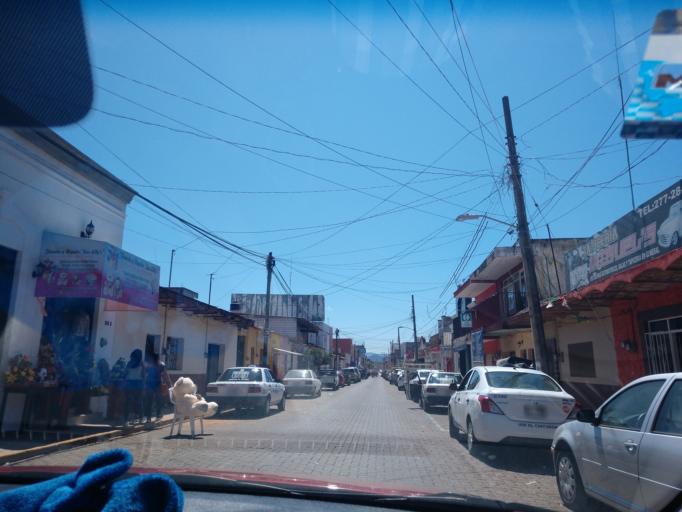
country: MX
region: Nayarit
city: Compostela
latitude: 21.2429
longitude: -104.9010
